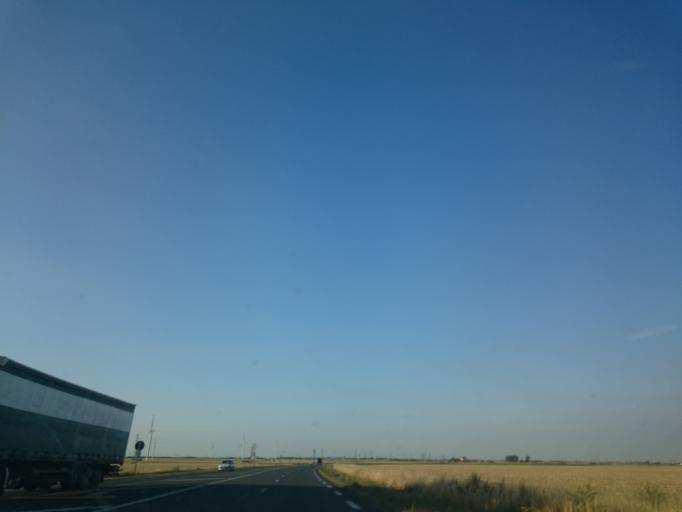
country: FR
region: Centre
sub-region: Departement d'Eure-et-Loir
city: Toury
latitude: 48.1470
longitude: 1.9056
